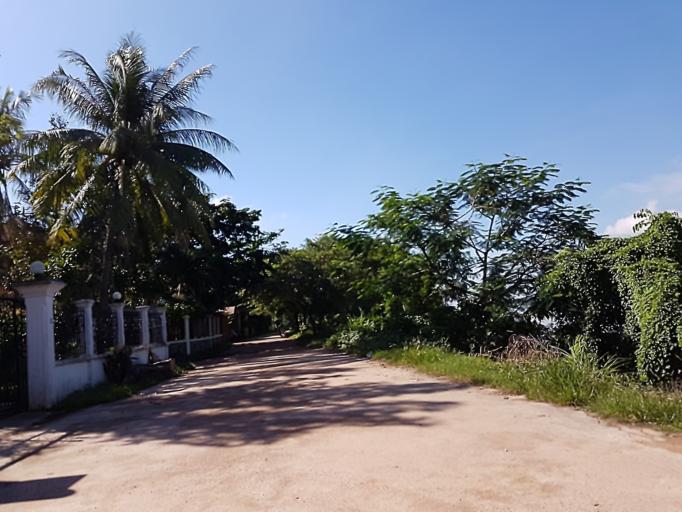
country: TH
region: Nong Khai
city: Si Chiang Mai
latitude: 17.9217
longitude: 102.6162
